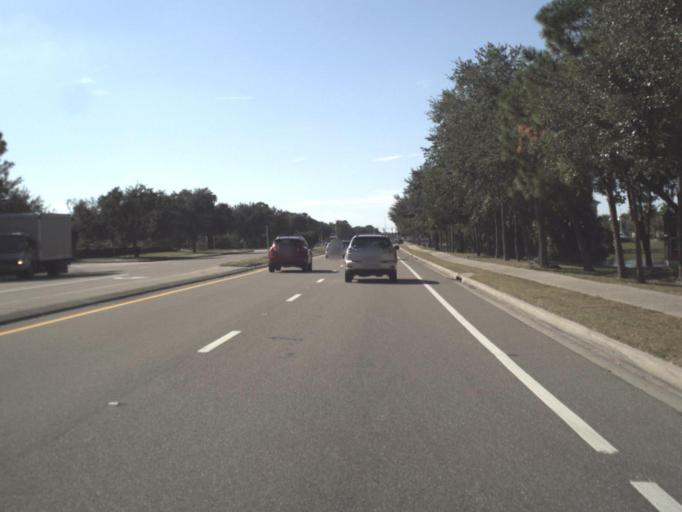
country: US
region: Florida
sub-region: Brevard County
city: South Patrick Shores
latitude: 28.2306
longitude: -80.7082
